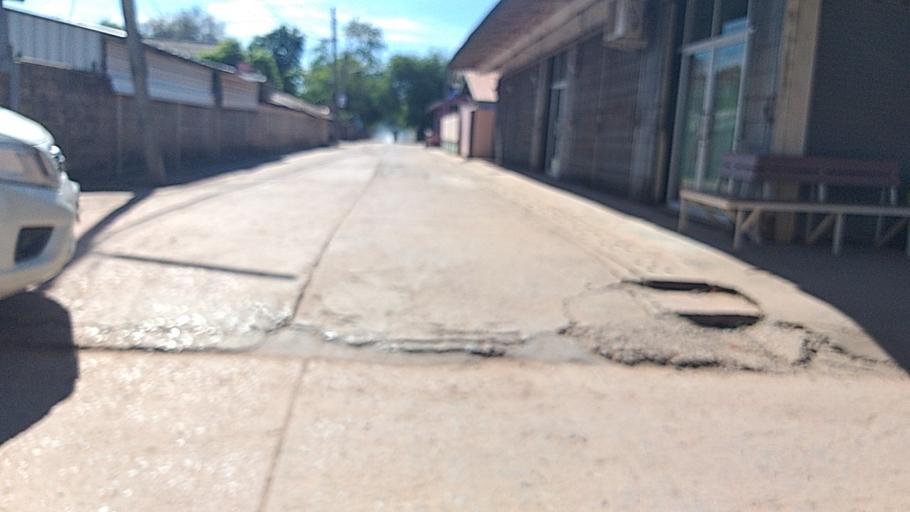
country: TH
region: Chaiyaphum
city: Ban Thaen
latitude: 16.4079
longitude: 102.3516
